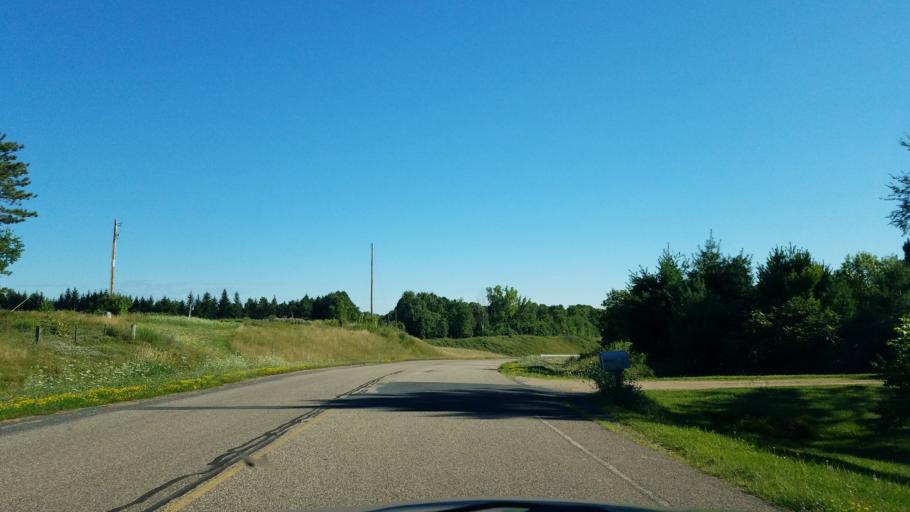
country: US
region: Wisconsin
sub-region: Saint Croix County
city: Somerset
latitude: 45.1081
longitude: -92.7268
